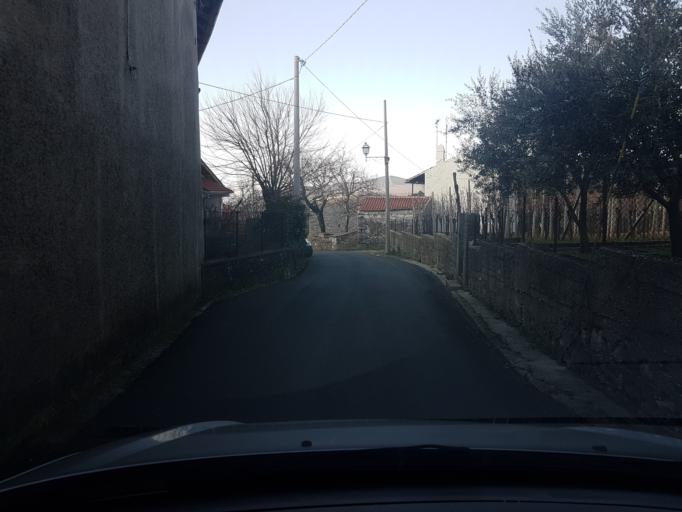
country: IT
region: Friuli Venezia Giulia
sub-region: Provincia di Trieste
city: Aurisina Cave
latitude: 45.7708
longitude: 13.6660
